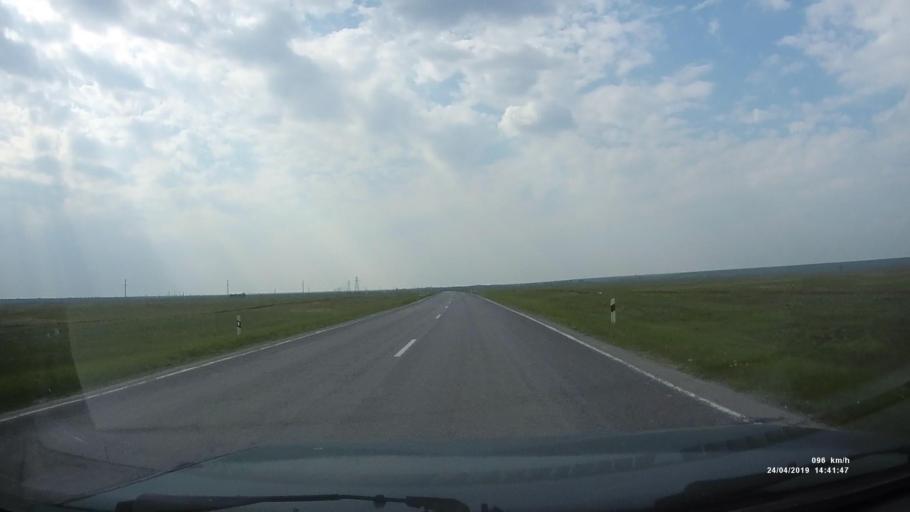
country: RU
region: Rostov
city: Remontnoye
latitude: 46.4480
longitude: 43.8745
